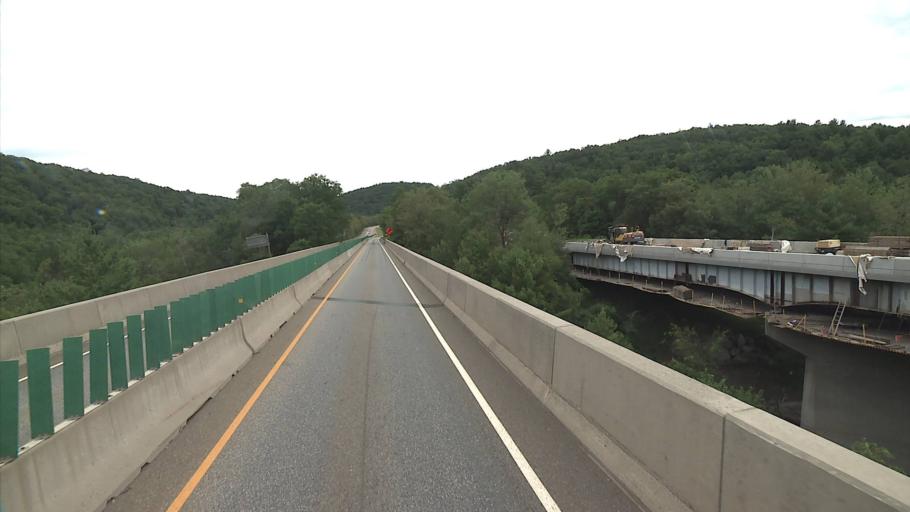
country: US
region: Connecticut
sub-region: Litchfield County
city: Northwest Harwinton
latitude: 41.7387
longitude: -73.1111
